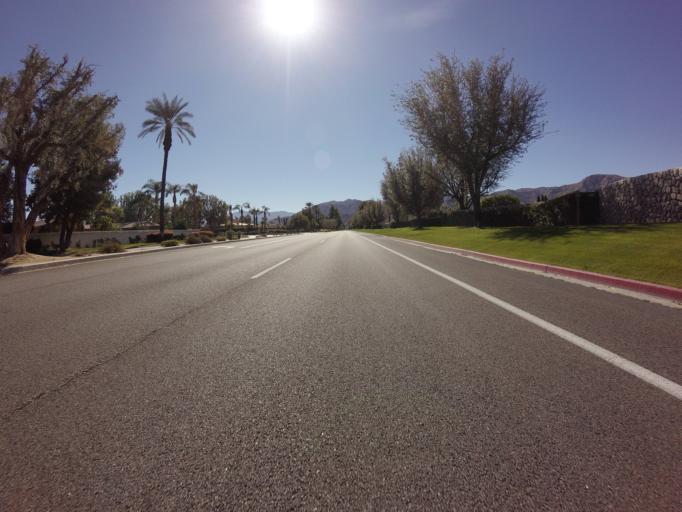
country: US
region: California
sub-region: Riverside County
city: Rancho Mirage
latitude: 33.7712
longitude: -116.4257
